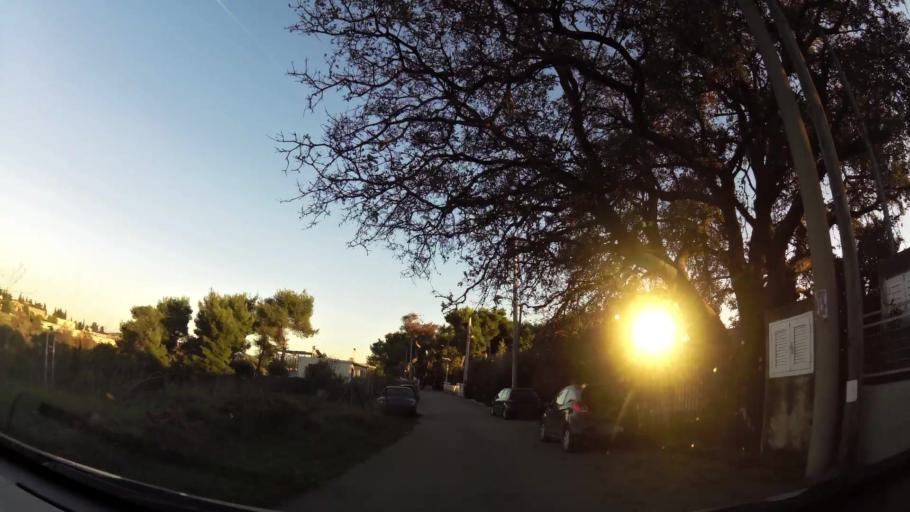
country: GR
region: Attica
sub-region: Nomarchia Anatolikis Attikis
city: Kryoneri
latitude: 38.1479
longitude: 23.8400
